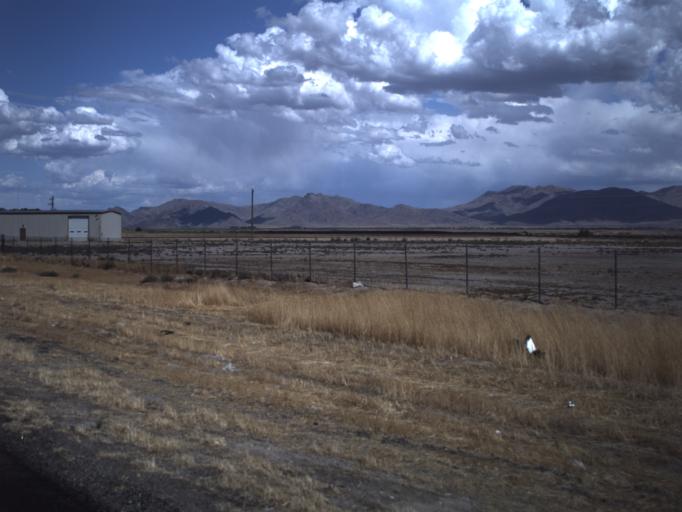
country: US
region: Utah
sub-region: Millard County
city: Delta
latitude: 39.5103
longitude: -112.3795
